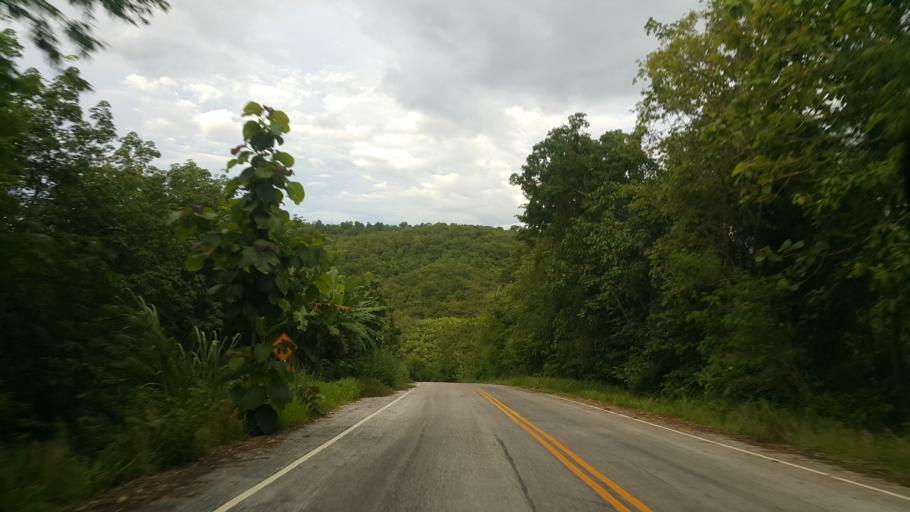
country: TH
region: Loei
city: Na Haeo
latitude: 17.4786
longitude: 101.1100
